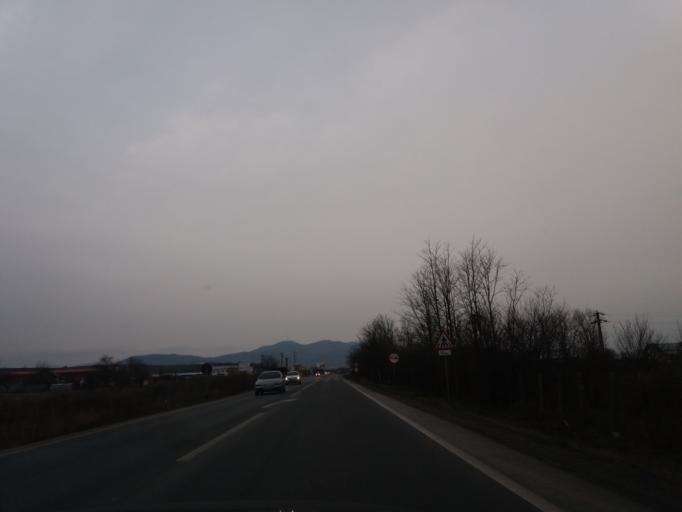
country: RO
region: Hunedoara
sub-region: Municipiul Deva
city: Cristur
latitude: 45.8528
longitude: 22.9681
